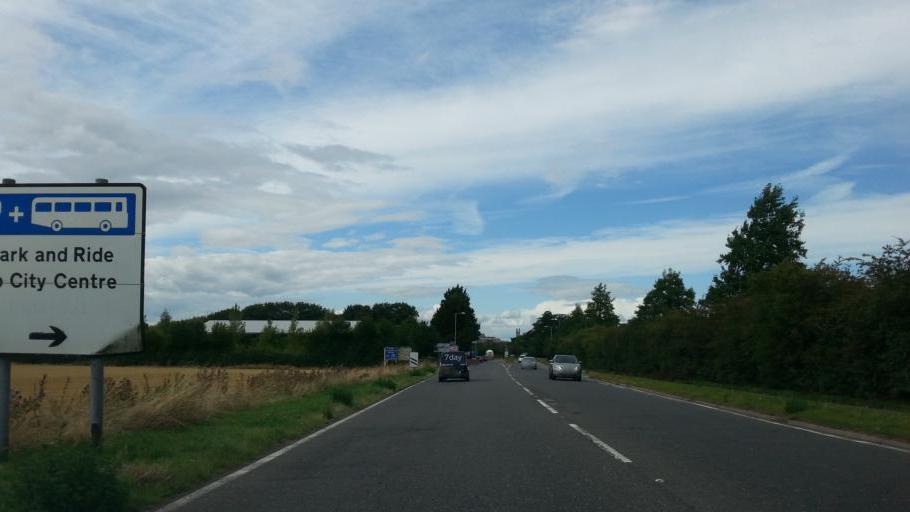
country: GB
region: England
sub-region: Cambridgeshire
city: Sawston
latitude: 52.1640
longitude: 0.1644
